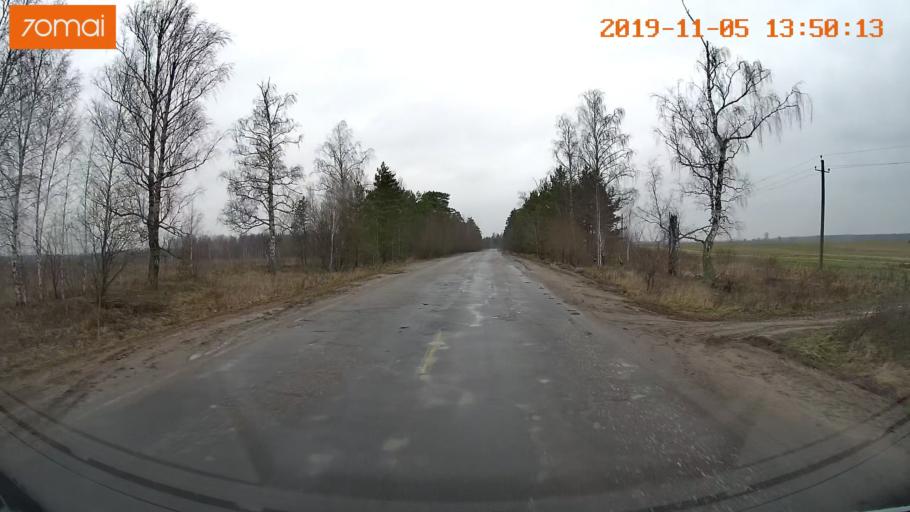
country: RU
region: Ivanovo
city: Kaminskiy
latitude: 57.0178
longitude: 41.4090
